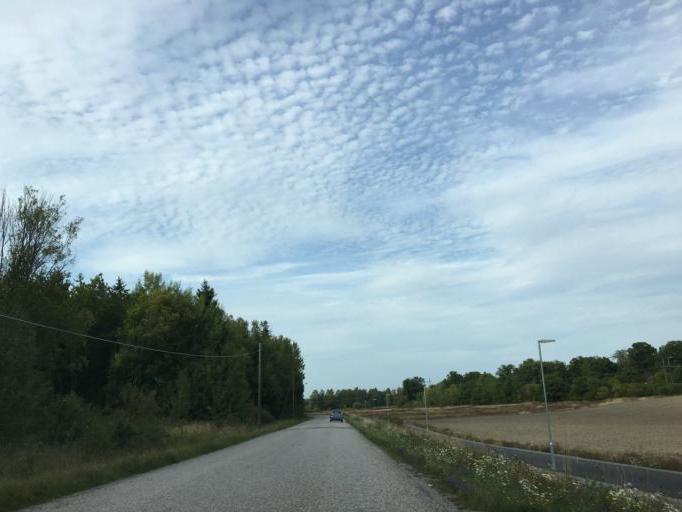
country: SE
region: Soedermanland
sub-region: Eskilstuna Kommun
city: Torshalla
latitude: 59.4468
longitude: 16.4689
